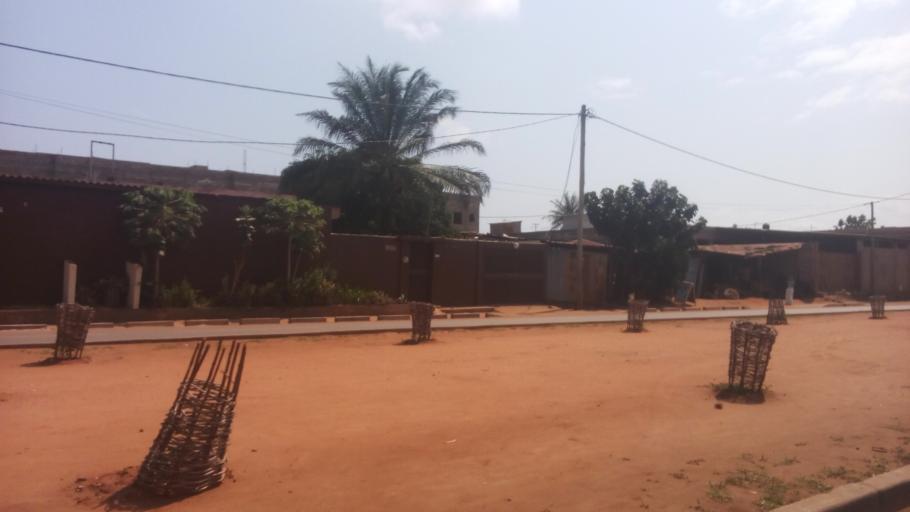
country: TG
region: Maritime
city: Lome
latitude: 6.1939
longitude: 1.2413
